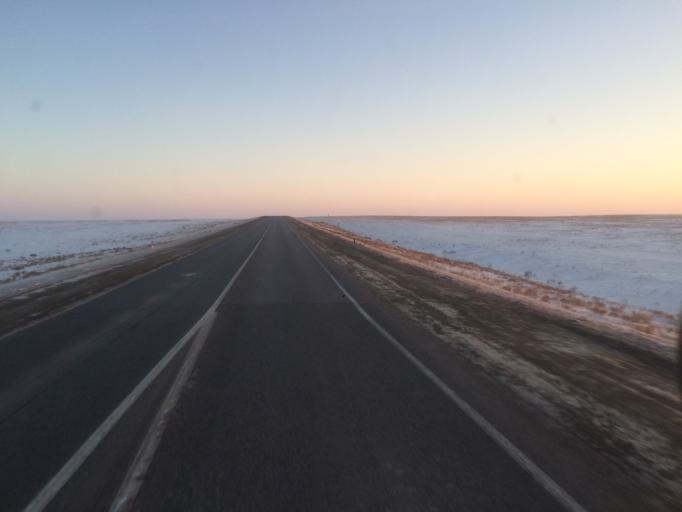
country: KZ
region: Qyzylorda
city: Sekseuil
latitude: 47.5721
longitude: 61.5112
